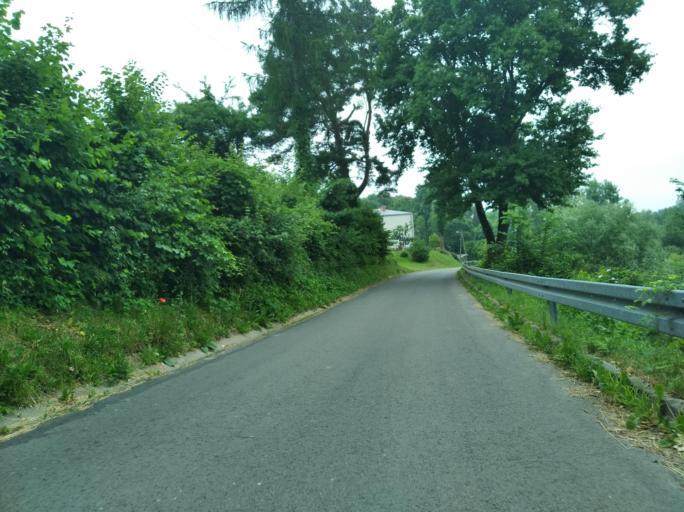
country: PL
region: Subcarpathian Voivodeship
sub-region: Powiat brzozowski
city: Haczow
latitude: 49.6792
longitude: 21.8905
